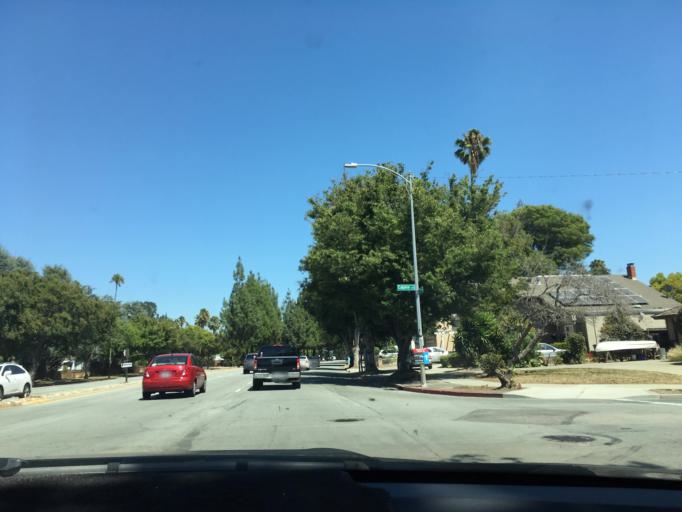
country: US
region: California
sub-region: Santa Clara County
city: Seven Trees
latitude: 37.2514
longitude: -121.8130
